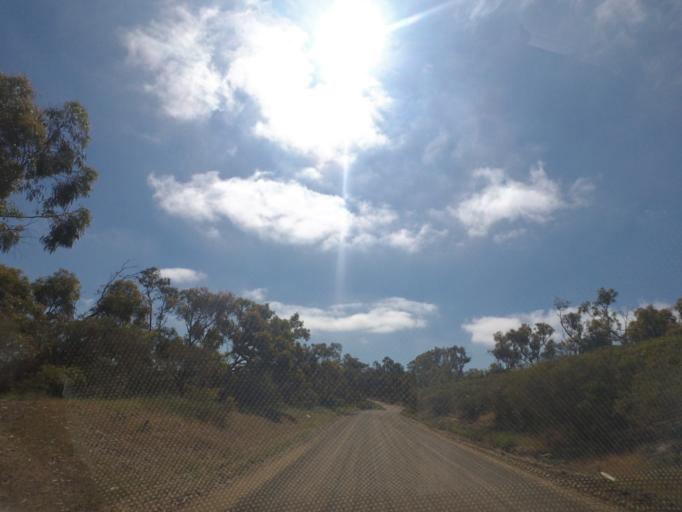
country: AU
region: Victoria
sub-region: Hume
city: Craigieburn
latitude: -37.4307
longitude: 144.9426
